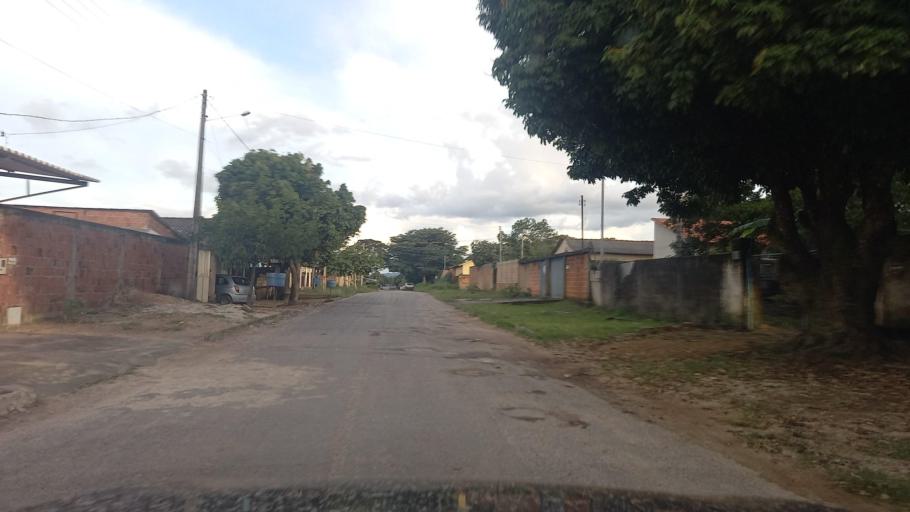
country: BR
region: Goias
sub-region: Cavalcante
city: Cavalcante
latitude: -13.7889
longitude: -47.4595
